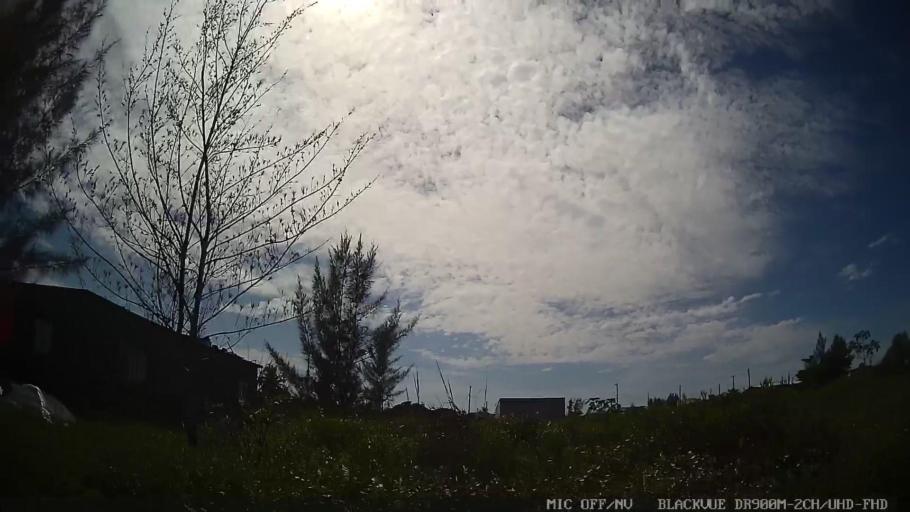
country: BR
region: Sao Paulo
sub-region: Iguape
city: Iguape
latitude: -24.7817
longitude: -47.6081
